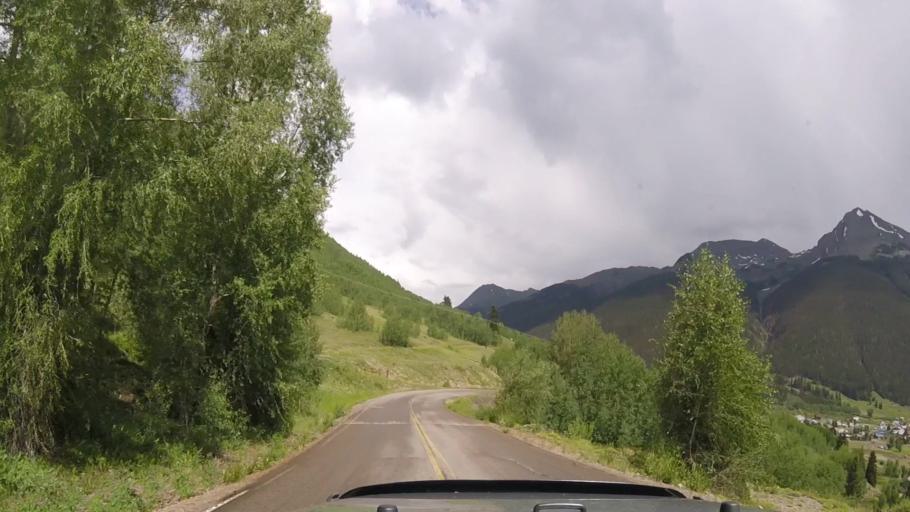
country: US
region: Colorado
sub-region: San Juan County
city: Silverton
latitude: 37.8207
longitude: -107.6624
